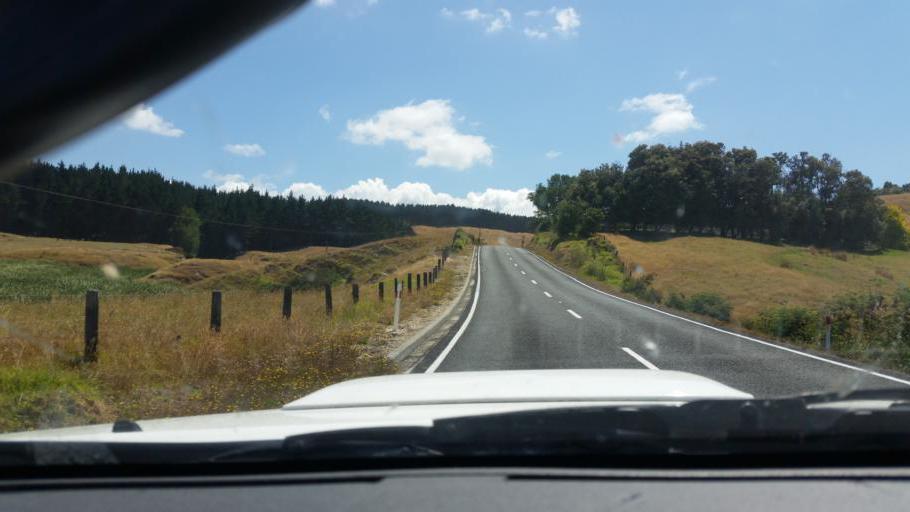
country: NZ
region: Northland
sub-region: Kaipara District
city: Dargaville
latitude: -35.8244
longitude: 173.6791
